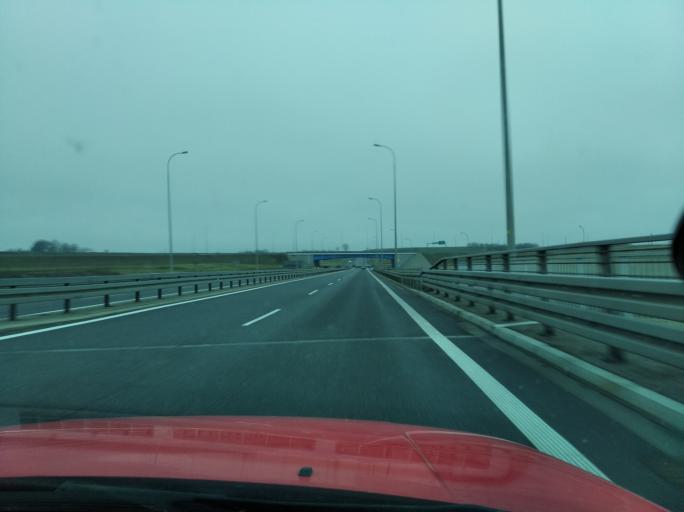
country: PL
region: Subcarpathian Voivodeship
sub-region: Powiat przeworski
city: Mirocin
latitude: 50.0375
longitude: 22.5772
